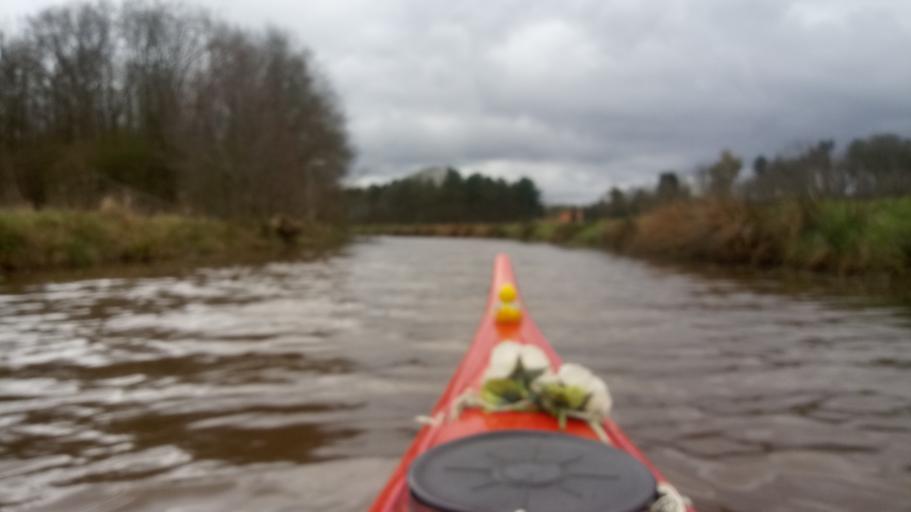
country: NL
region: Groningen
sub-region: Gemeente Vlagtwedde
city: Sellingen
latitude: 52.9646
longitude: 7.1404
